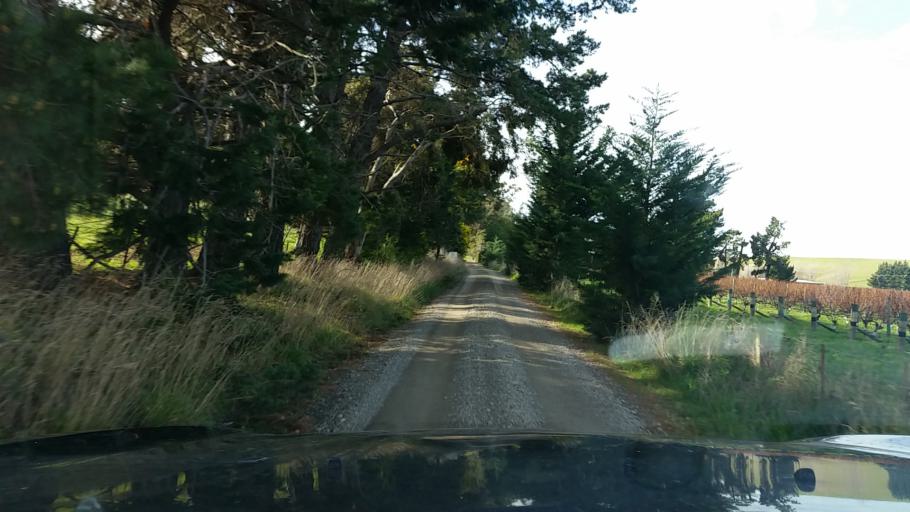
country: NZ
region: Marlborough
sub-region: Marlborough District
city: Blenheim
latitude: -41.5973
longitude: 174.1370
